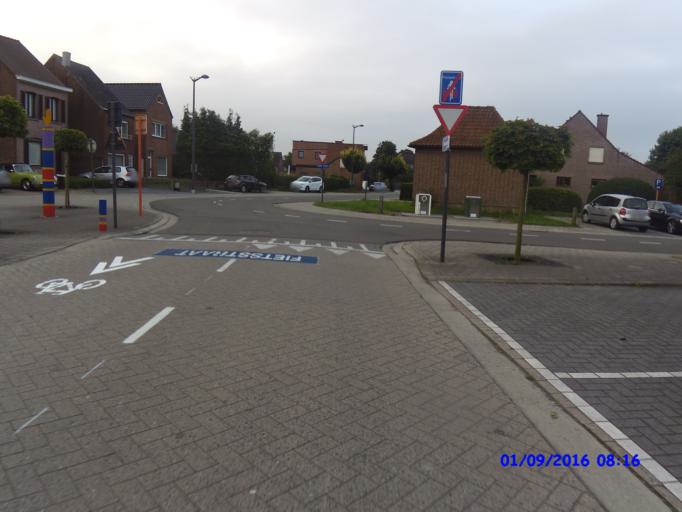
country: BE
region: Flanders
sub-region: Provincie Antwerpen
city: Bonheiden
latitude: 51.0366
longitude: 4.5311
